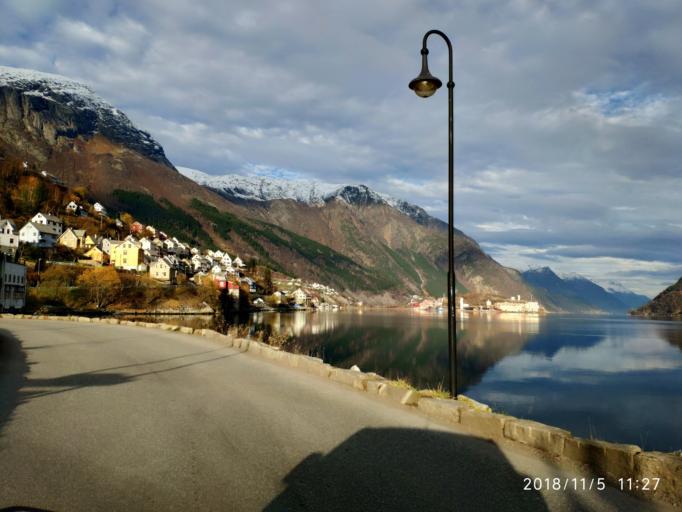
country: NO
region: Hordaland
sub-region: Odda
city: Odda
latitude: 60.0707
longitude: 6.5420
